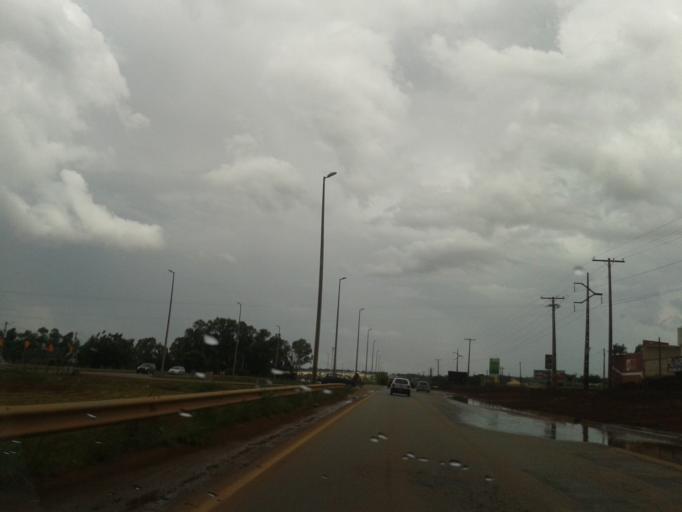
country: BR
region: Goias
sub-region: Goianira
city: Goianira
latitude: -16.5808
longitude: -49.3878
